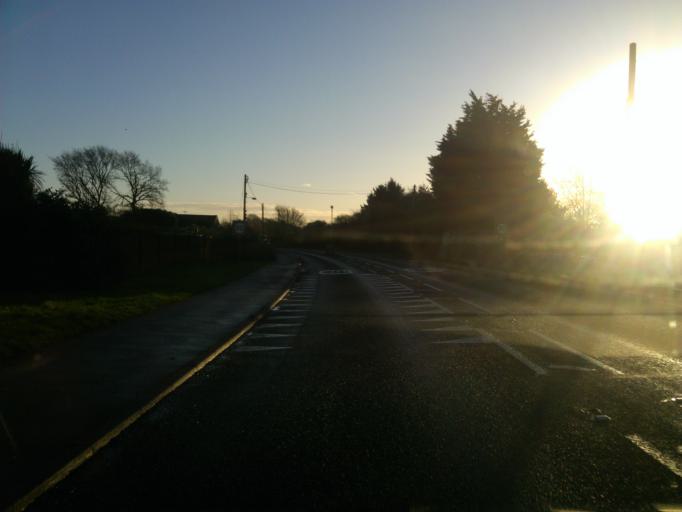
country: GB
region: England
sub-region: Essex
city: Great Bentley
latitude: 51.8413
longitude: 1.0346
